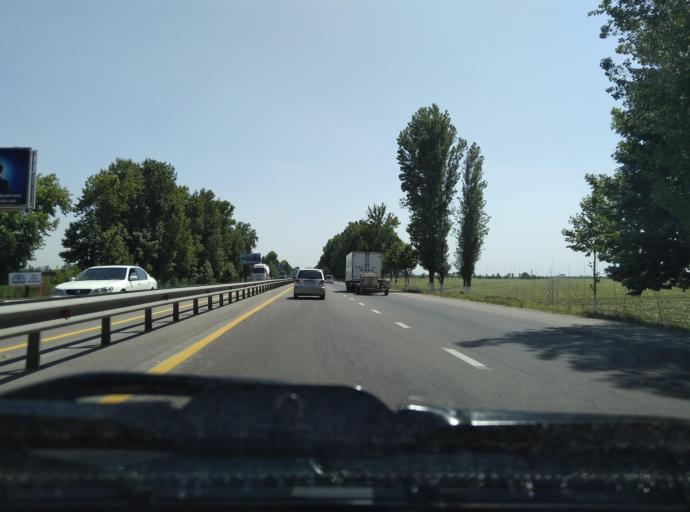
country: UZ
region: Toshkent Shahri
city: Bektemir
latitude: 41.2348
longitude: 69.4021
